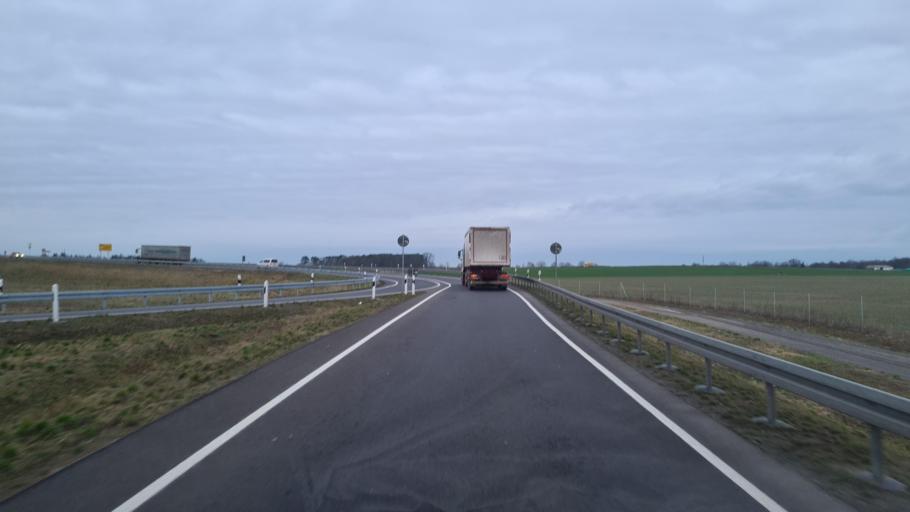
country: DE
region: Brandenburg
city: Stahnsdorf
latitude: 52.3633
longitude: 13.2391
